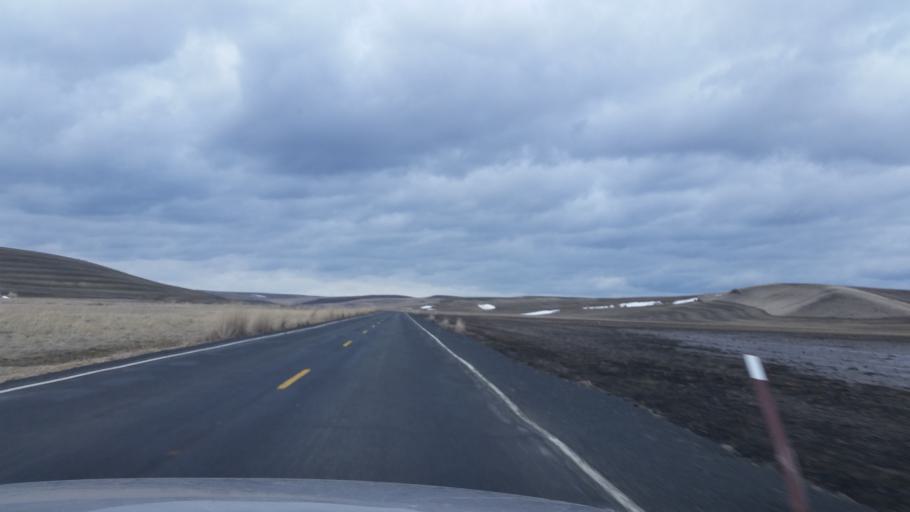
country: US
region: Washington
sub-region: Spokane County
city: Cheney
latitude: 47.1682
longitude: -117.8700
